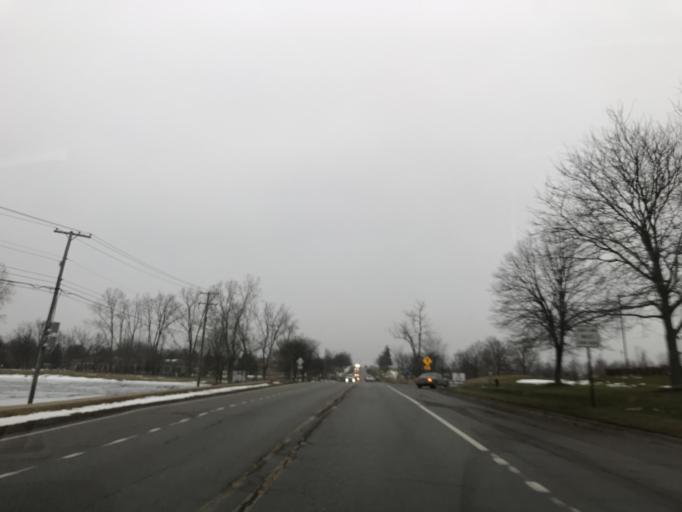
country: US
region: Michigan
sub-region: Oakland County
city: South Lyon
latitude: 42.4660
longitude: -83.6517
